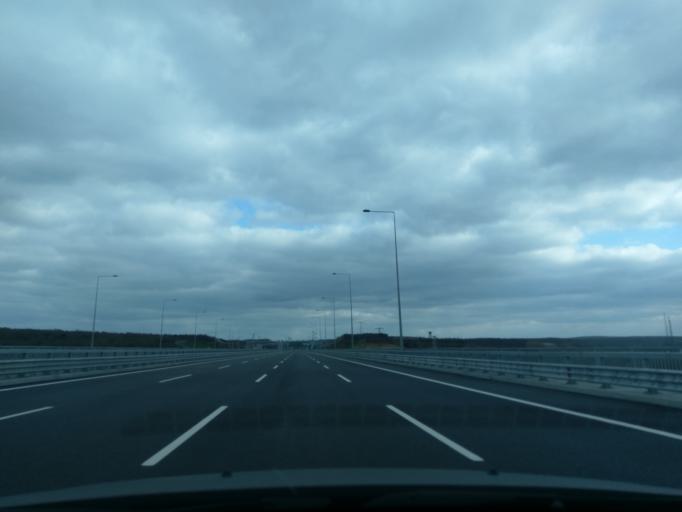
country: TR
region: Istanbul
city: Kemerburgaz
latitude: 41.2375
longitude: 28.8114
